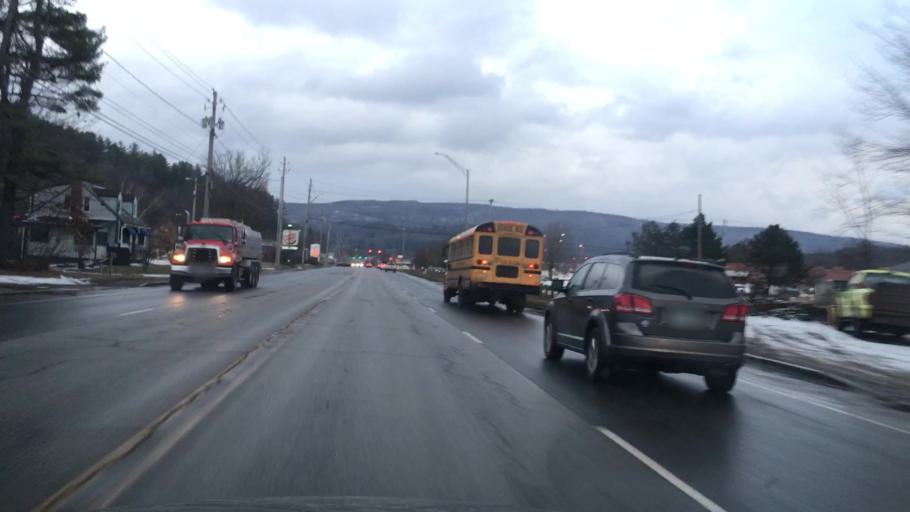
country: US
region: New Hampshire
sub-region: Sullivan County
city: Claremont
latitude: 43.3665
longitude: -72.3220
